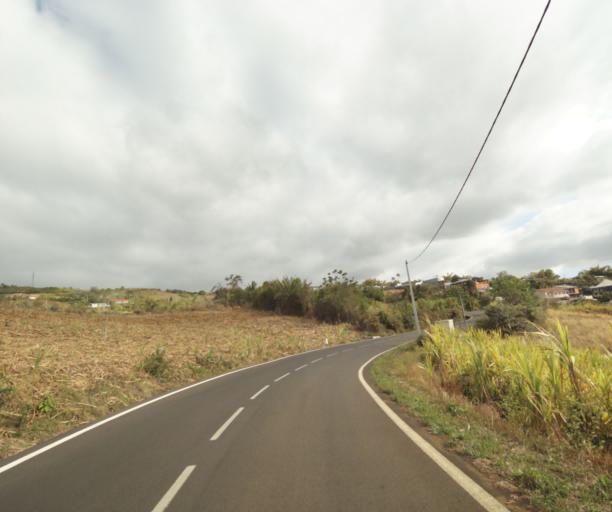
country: RE
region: Reunion
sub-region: Reunion
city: Saint-Paul
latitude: -21.0275
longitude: 55.3120
